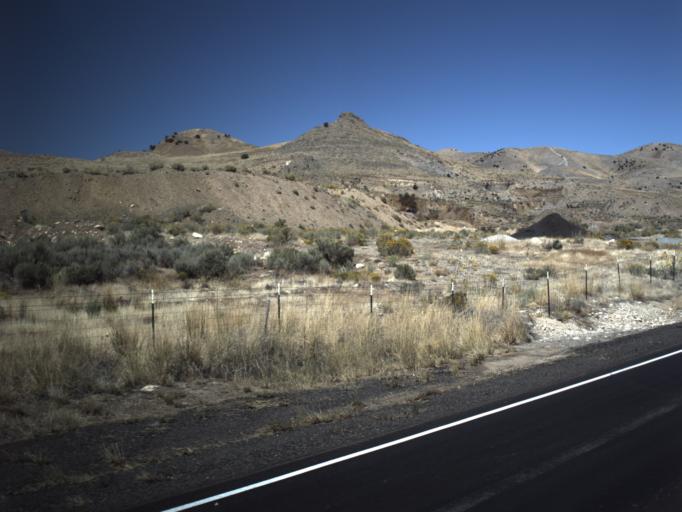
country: US
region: Utah
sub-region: Utah County
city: Saratoga Springs
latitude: 40.2141
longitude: -111.8877
